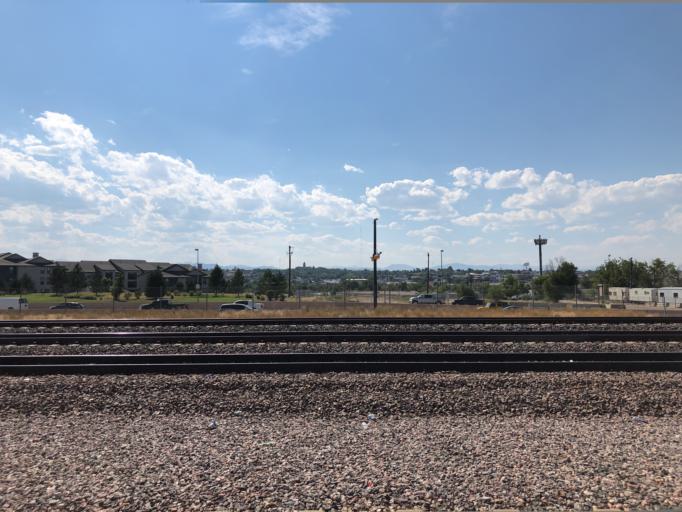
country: US
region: Colorado
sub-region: Arapahoe County
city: Englewood
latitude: 39.6556
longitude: -104.9998
